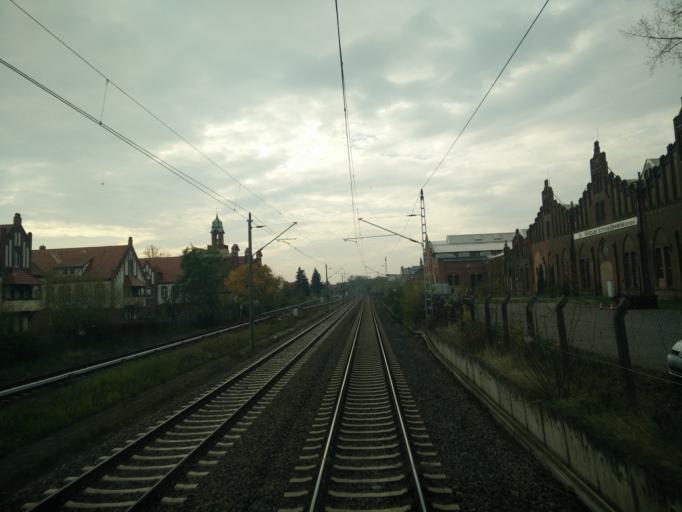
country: DE
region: Brandenburg
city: Wildau
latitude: 52.3228
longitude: 13.6350
